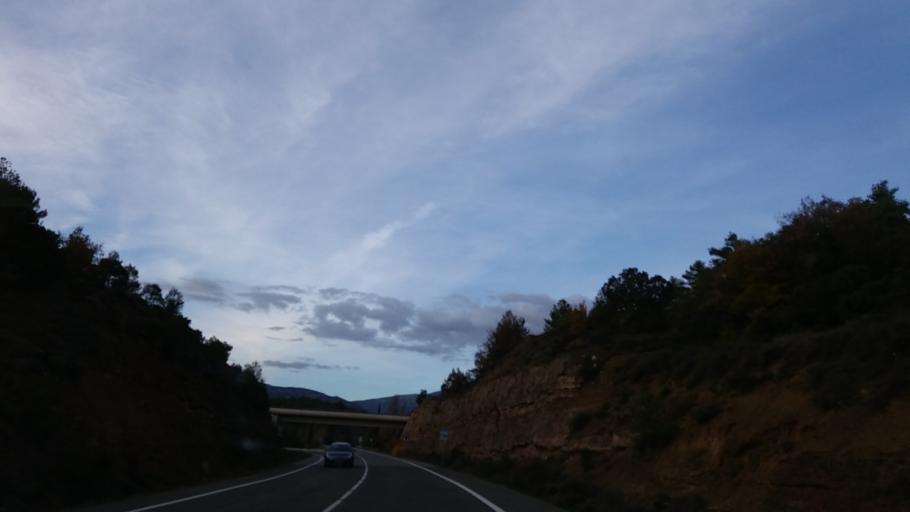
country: ES
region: Catalonia
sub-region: Provincia de Lleida
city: Tiurana
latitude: 41.9977
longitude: 1.2967
